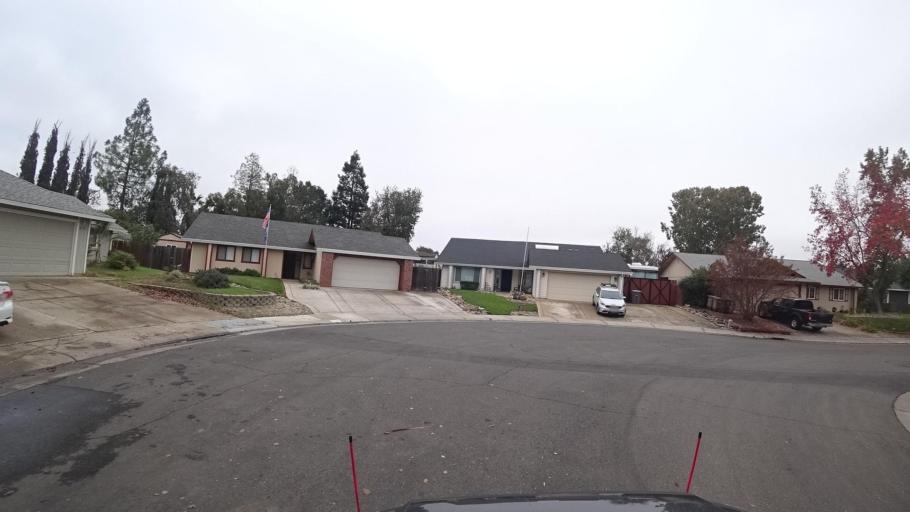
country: US
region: California
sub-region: Sacramento County
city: Elk Grove
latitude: 38.3951
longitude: -121.3605
